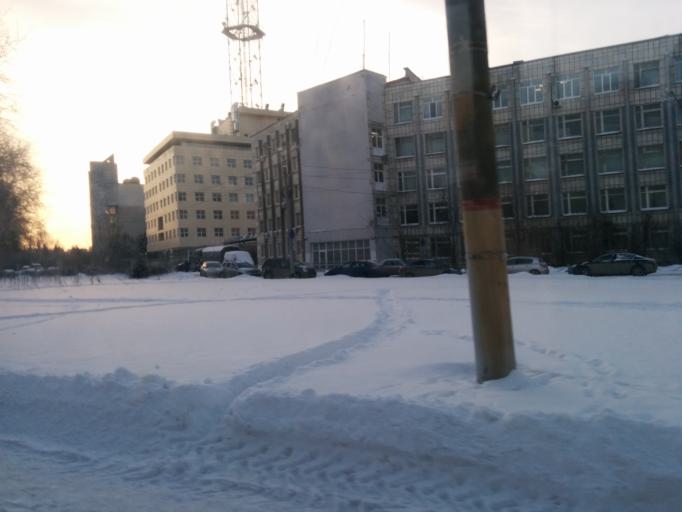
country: RU
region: Perm
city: Perm
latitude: 57.9945
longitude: 56.2871
